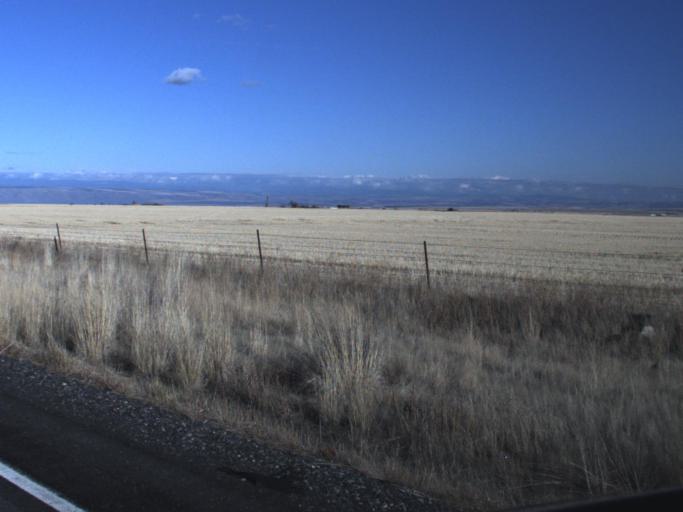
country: US
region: Washington
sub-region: Asotin County
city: Asotin
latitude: 46.1807
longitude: -117.0811
